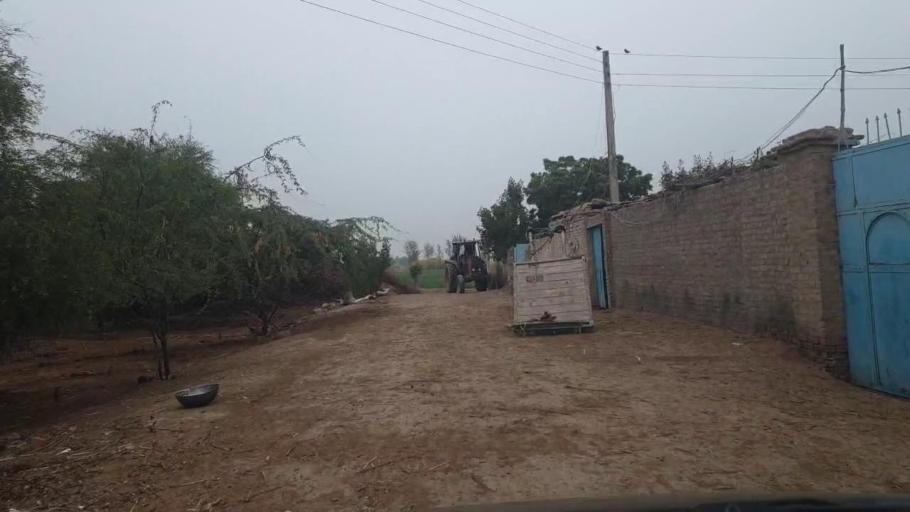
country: PK
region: Sindh
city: Tando Adam
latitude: 25.8042
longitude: 68.6916
